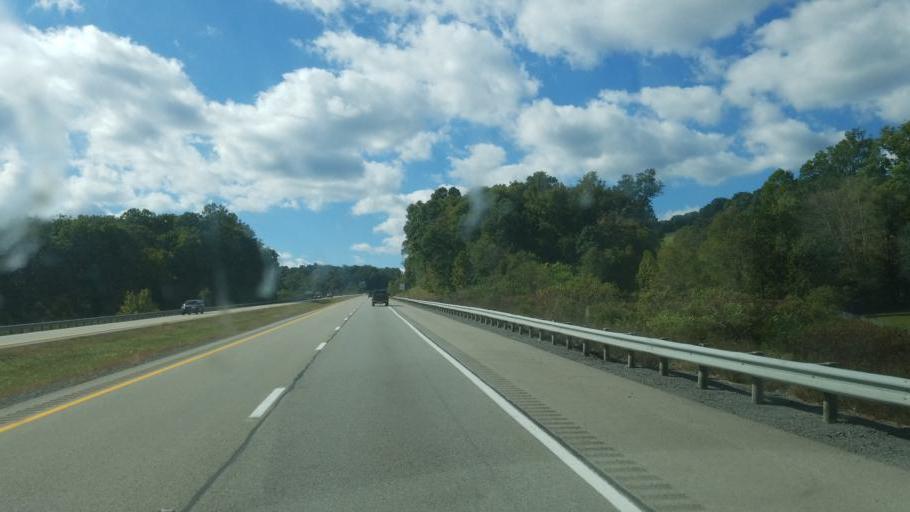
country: US
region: West Virginia
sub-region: Preston County
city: Kingwood
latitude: 39.6561
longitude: -79.6477
